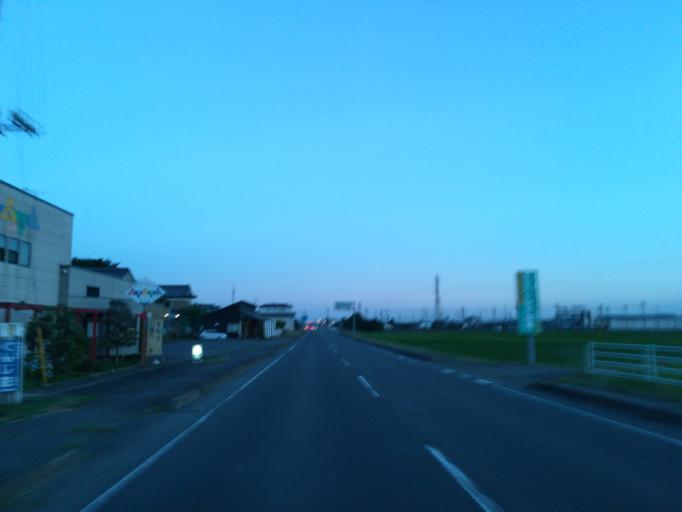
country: JP
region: Ibaraki
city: Tsukuba
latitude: 36.2286
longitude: 140.0647
